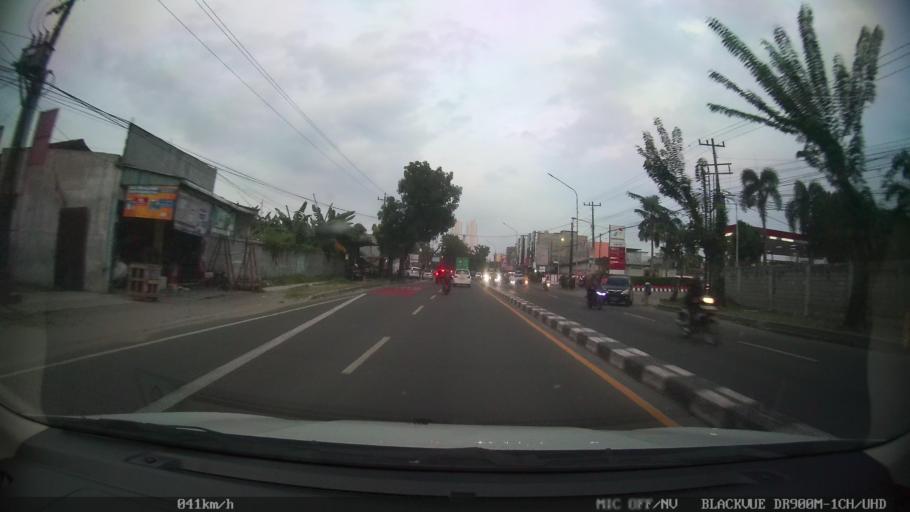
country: ID
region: North Sumatra
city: Sunggal
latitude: 3.5952
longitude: 98.6161
